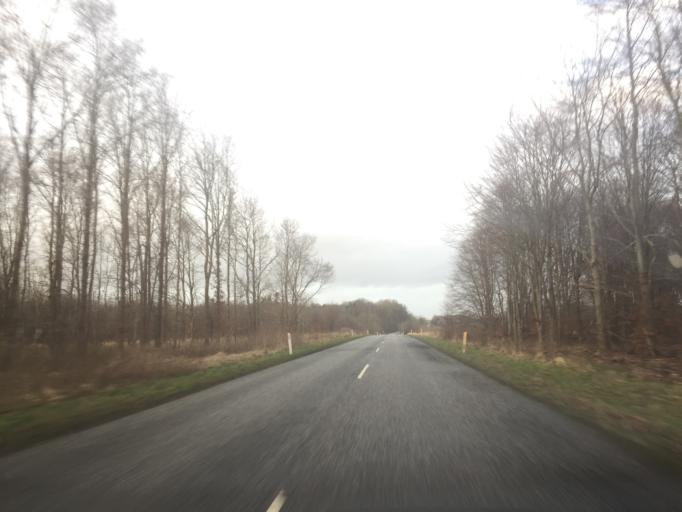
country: DK
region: Capital Region
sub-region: Egedal Kommune
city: Smorumnedre
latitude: 55.6950
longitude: 12.3229
